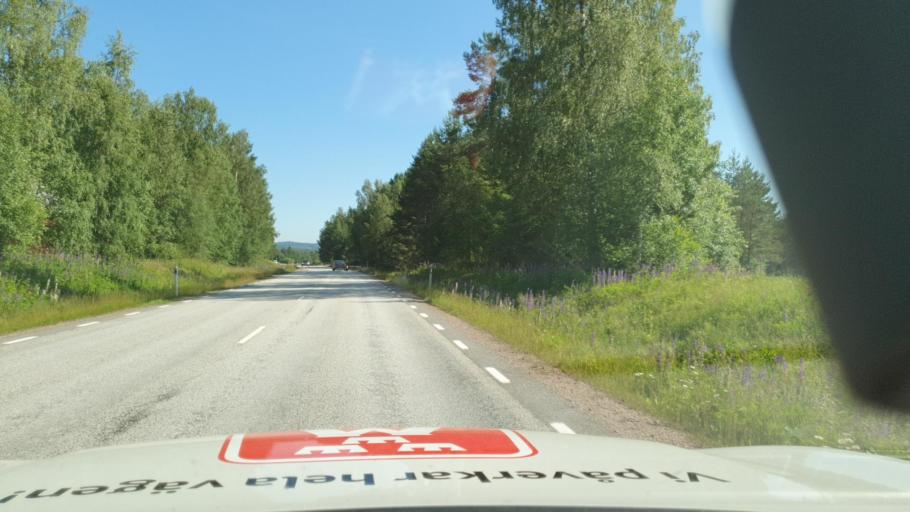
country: SE
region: Vaermland
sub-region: Storfors Kommun
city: Storfors
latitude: 59.5133
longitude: 14.3037
